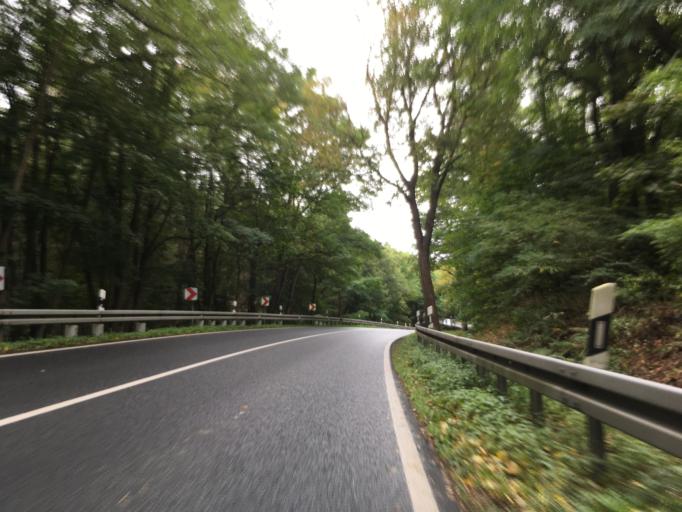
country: DE
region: Brandenburg
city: Werftpfuhl
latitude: 52.6876
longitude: 13.8541
